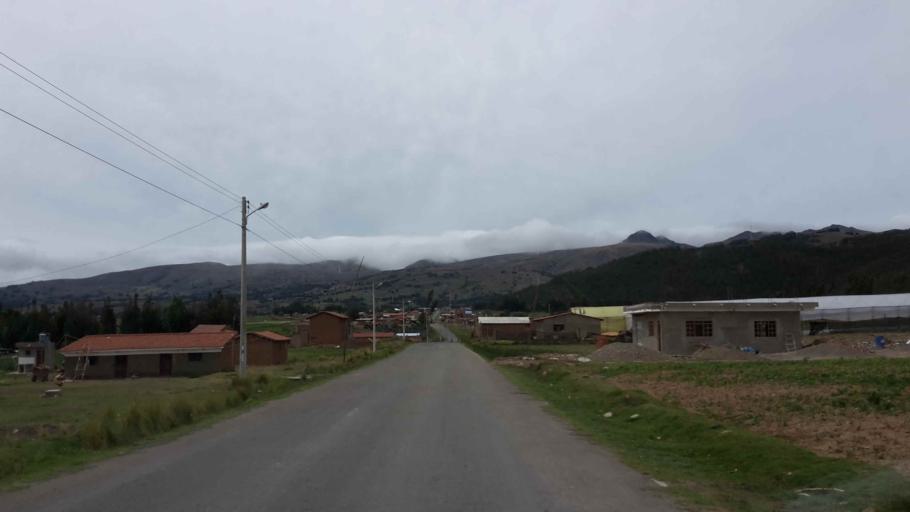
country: BO
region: Cochabamba
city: Arani
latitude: -17.4535
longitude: -65.7191
